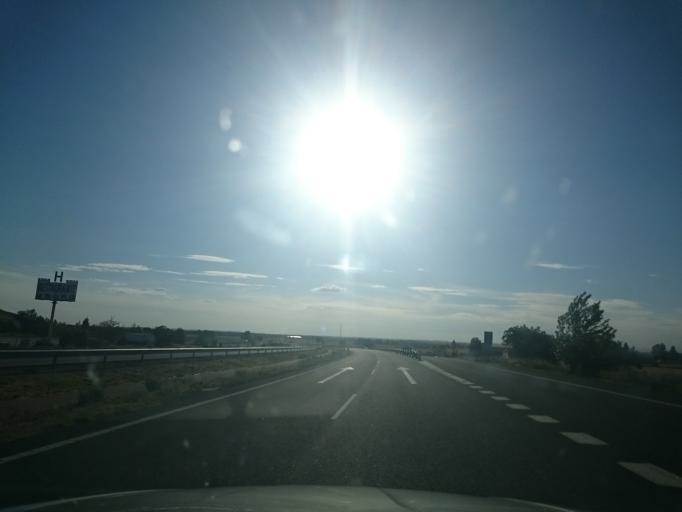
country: ES
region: Castille and Leon
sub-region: Provincia de Burgos
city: Sasamon
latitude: 42.4010
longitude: -4.0344
